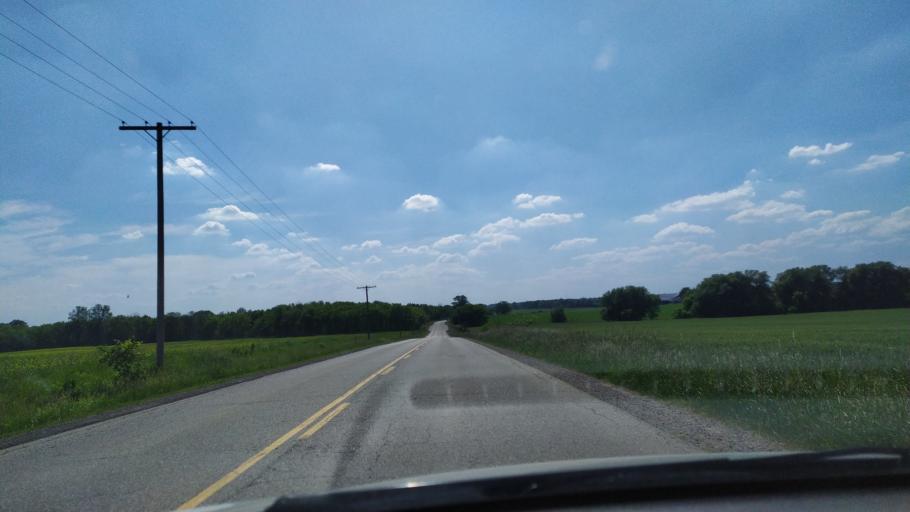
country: CA
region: Ontario
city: Kitchener
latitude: 43.3601
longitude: -80.6321
